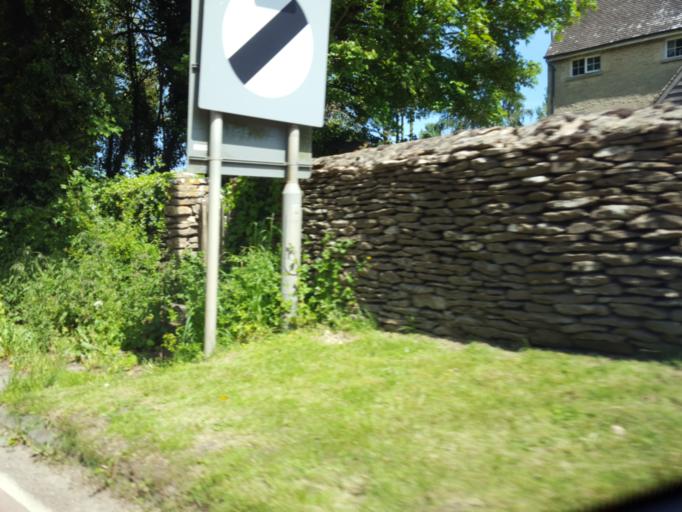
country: GB
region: England
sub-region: Wiltshire
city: Hankerton
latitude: 51.6365
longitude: -2.0657
